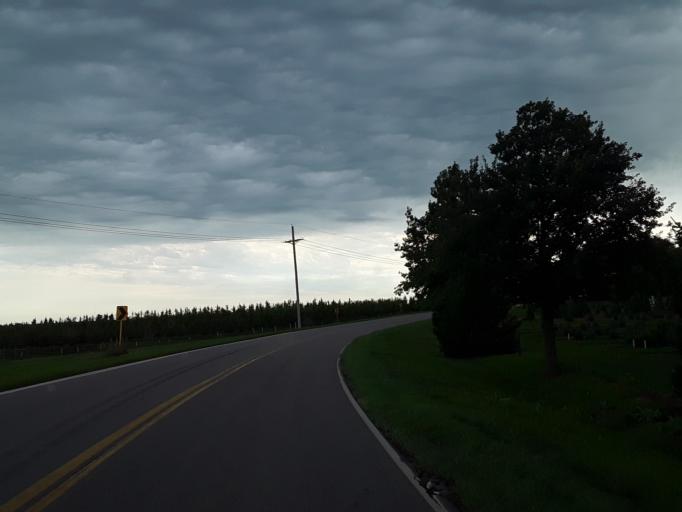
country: US
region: Nebraska
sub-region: Saunders County
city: Yutan
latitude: 41.1911
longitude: -96.3980
